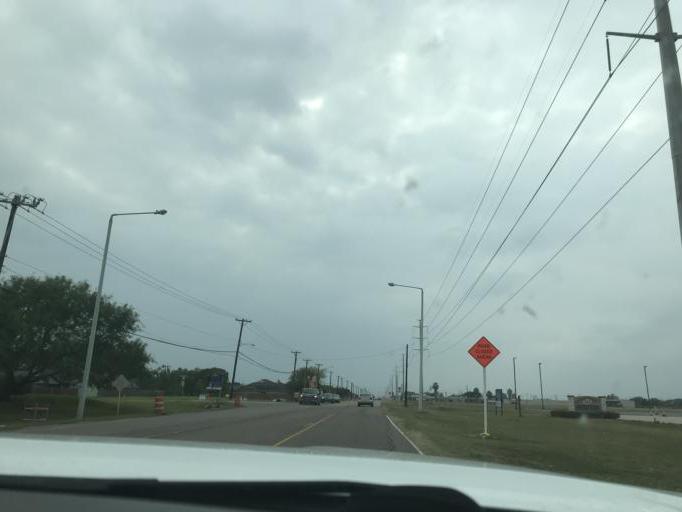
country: US
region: Texas
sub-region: Nueces County
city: Corpus Christi
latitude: 27.6700
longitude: -97.3562
